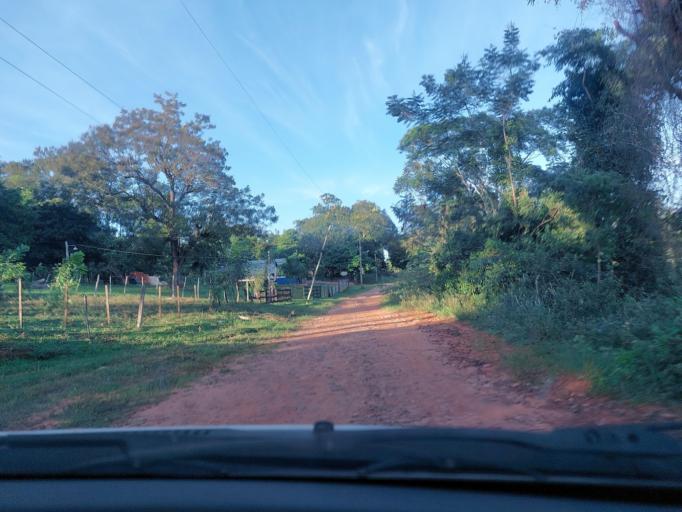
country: PY
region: San Pedro
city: Itacurubi del Rosario
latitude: -24.5545
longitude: -56.5882
